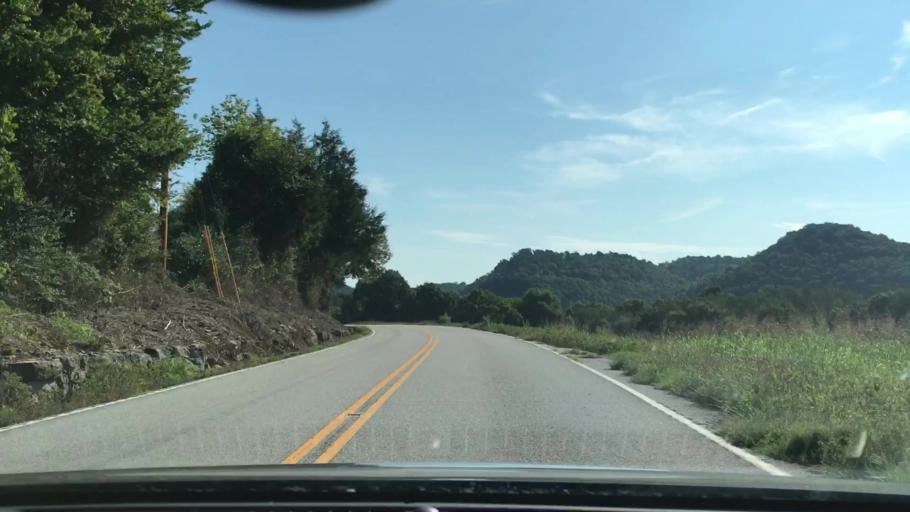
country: US
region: Tennessee
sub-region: Jackson County
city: Gainesboro
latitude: 36.3546
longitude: -85.7036
